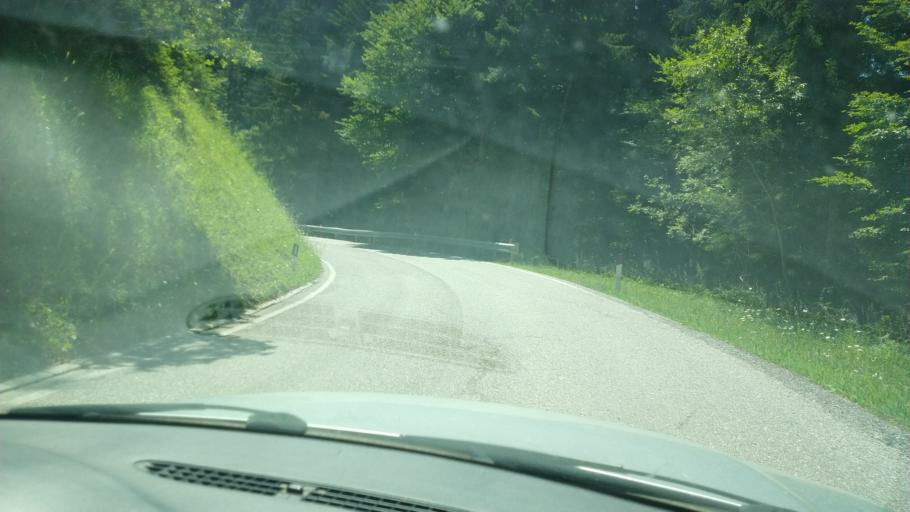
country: IT
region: Trentino-Alto Adige
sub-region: Provincia di Trento
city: Folgaria
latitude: 45.9025
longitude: 11.2119
